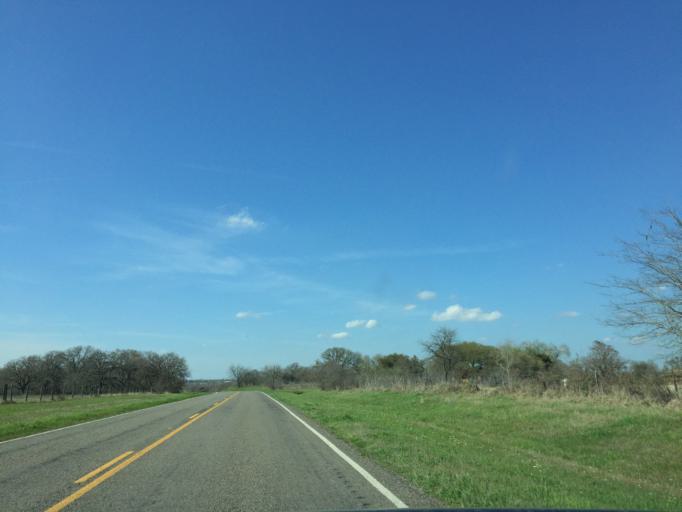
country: US
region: Texas
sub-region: Milam County
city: Thorndale
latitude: 30.5815
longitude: -97.1862
